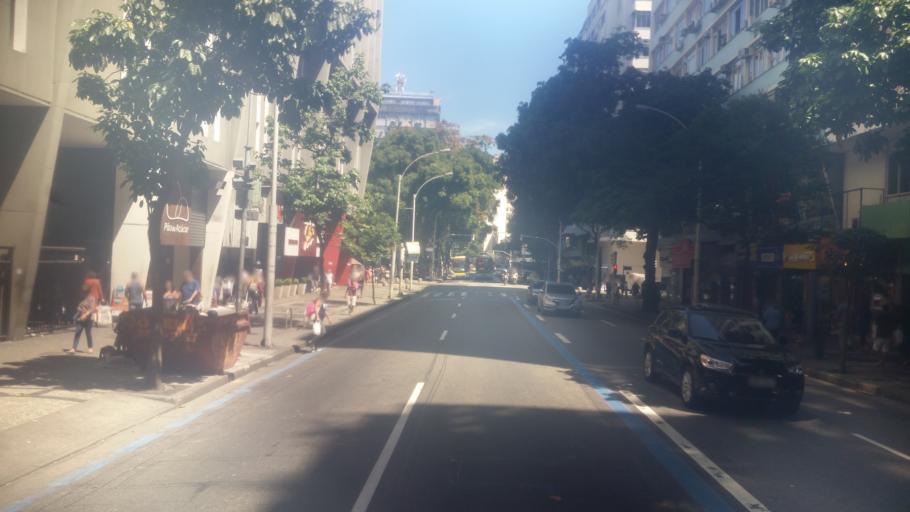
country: BR
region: Rio de Janeiro
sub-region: Rio De Janeiro
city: Rio de Janeiro
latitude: -22.9684
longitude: -43.1835
